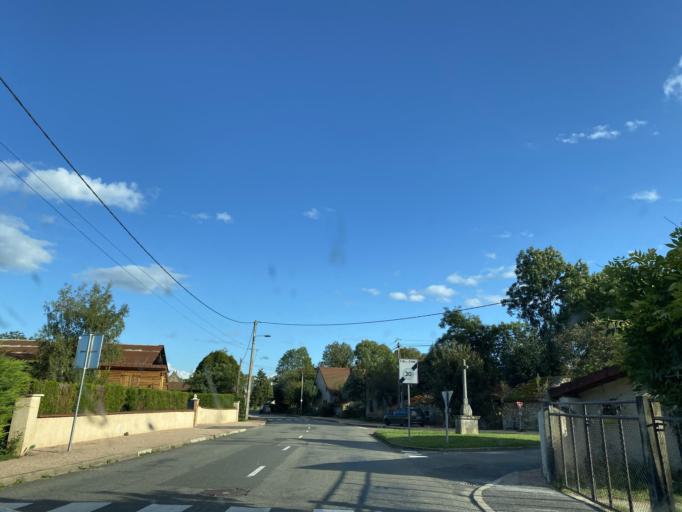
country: FR
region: Auvergne
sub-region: Departement de l'Allier
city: Gannat
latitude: 46.0760
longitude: 3.2739
